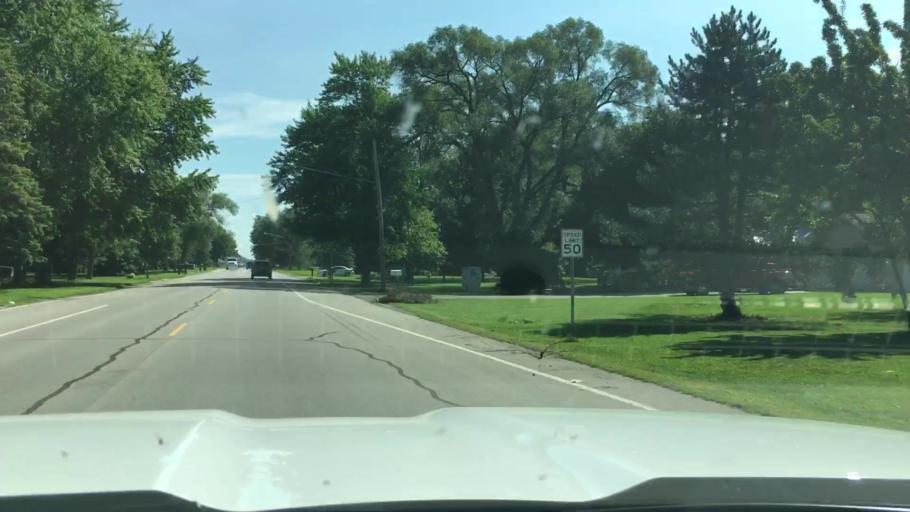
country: US
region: Michigan
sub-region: Bay County
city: Essexville
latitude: 43.5940
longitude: -83.8161
